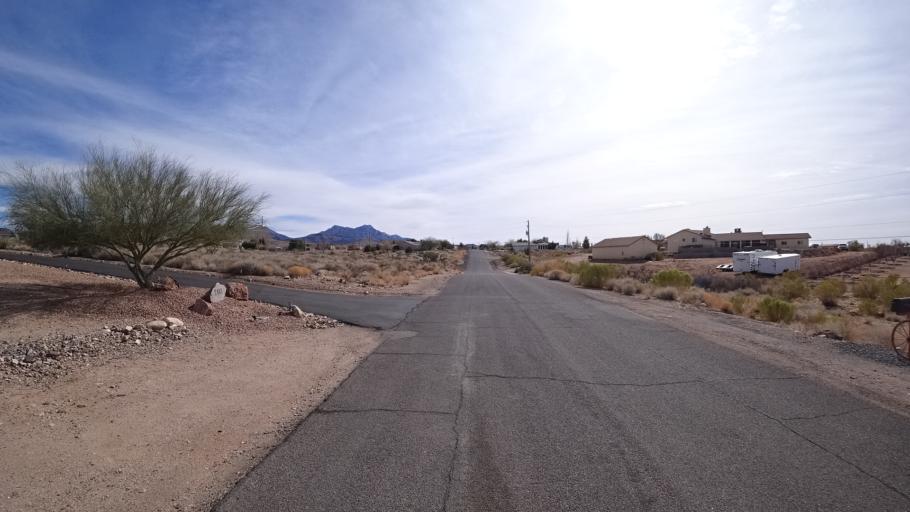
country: US
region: Arizona
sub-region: Mohave County
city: Kingman
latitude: 35.1908
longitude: -113.9869
